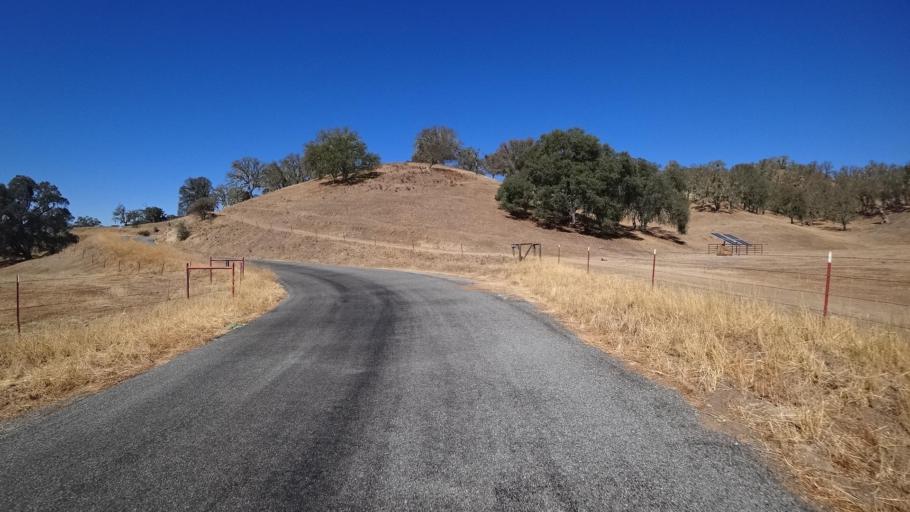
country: US
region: California
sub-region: Monterey County
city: Gonzales
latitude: 36.3963
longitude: -121.5733
